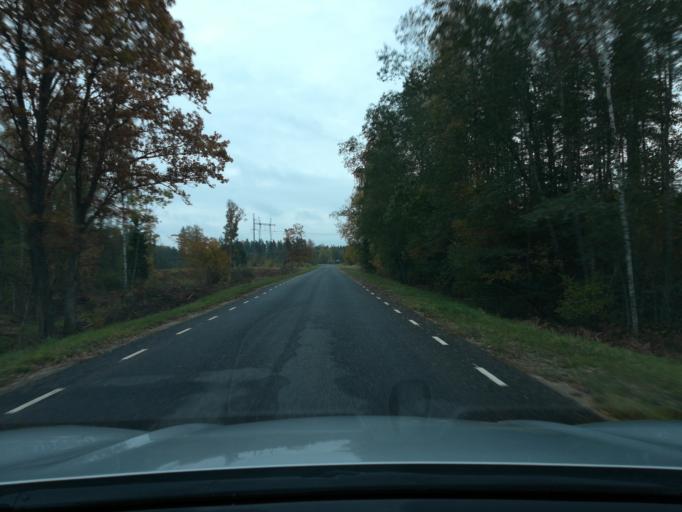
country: EE
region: Ida-Virumaa
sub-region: Johvi vald
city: Johvi
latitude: 59.0196
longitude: 27.4058
